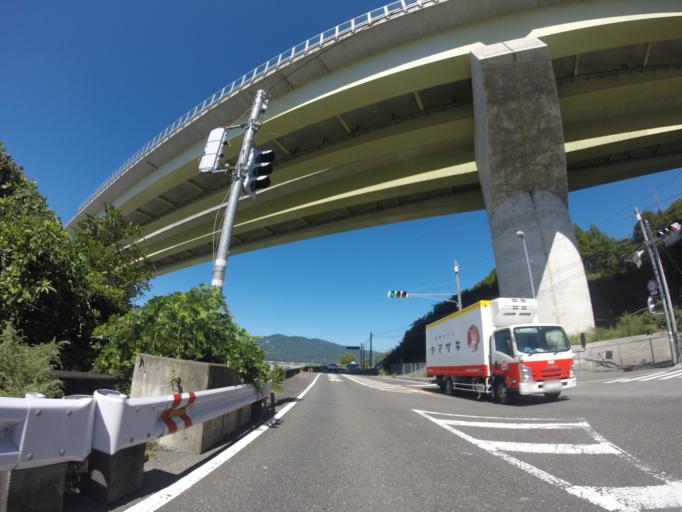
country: JP
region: Shizuoka
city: Kanaya
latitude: 34.8553
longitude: 138.1366
